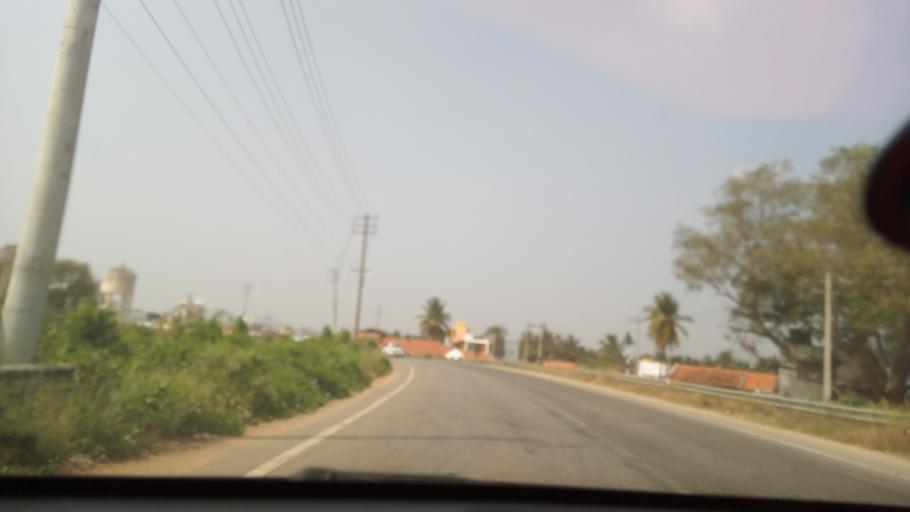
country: IN
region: Karnataka
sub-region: Chamrajnagar
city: Chamrajnagar
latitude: 11.9881
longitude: 76.8712
